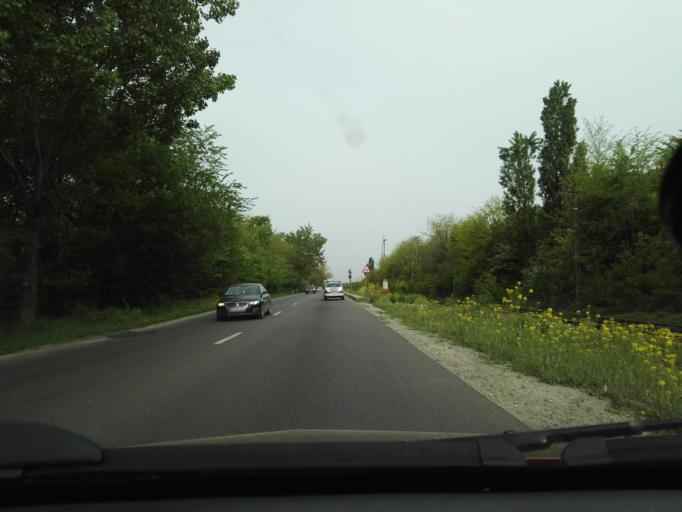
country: RO
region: Ilfov
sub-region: Comuna Magurele
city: Magurele
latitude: 44.3560
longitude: 26.0464
